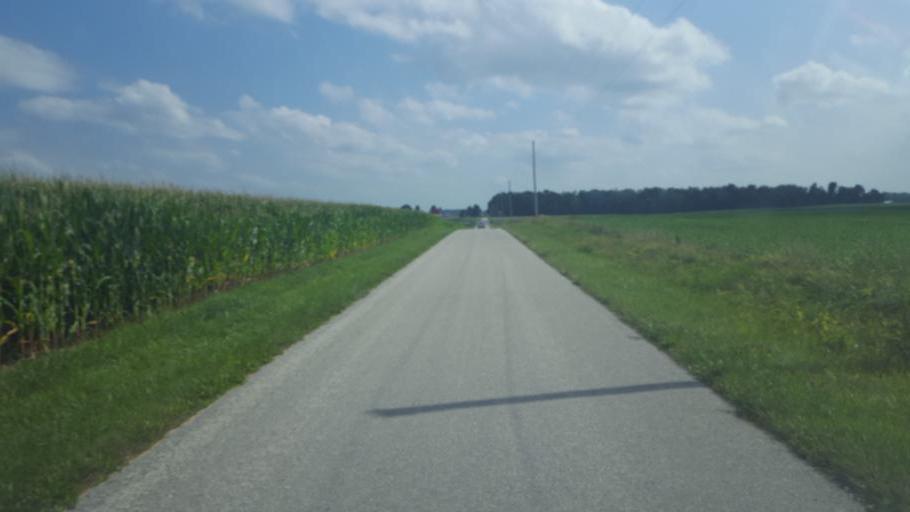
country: US
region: Ohio
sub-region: Huron County
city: Willard
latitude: 40.9812
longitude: -82.7625
